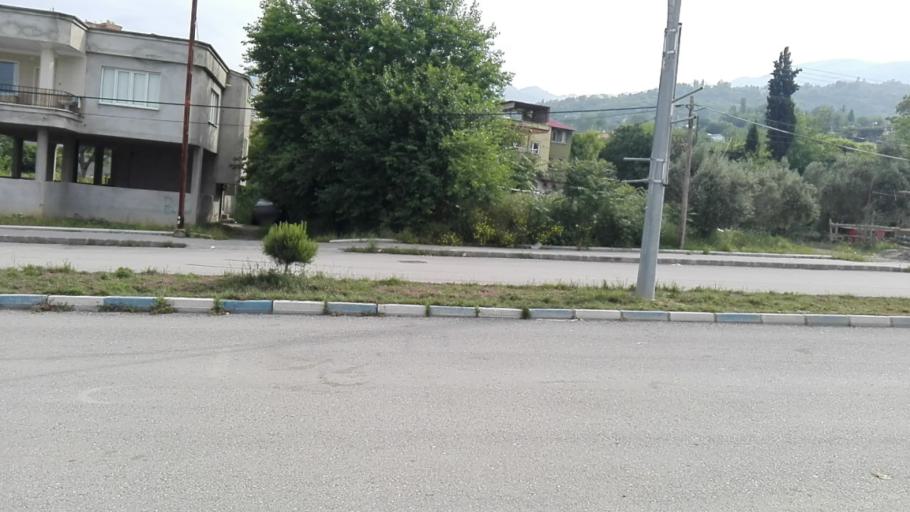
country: TR
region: Osmaniye
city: Haruniye
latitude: 37.2492
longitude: 36.4656
